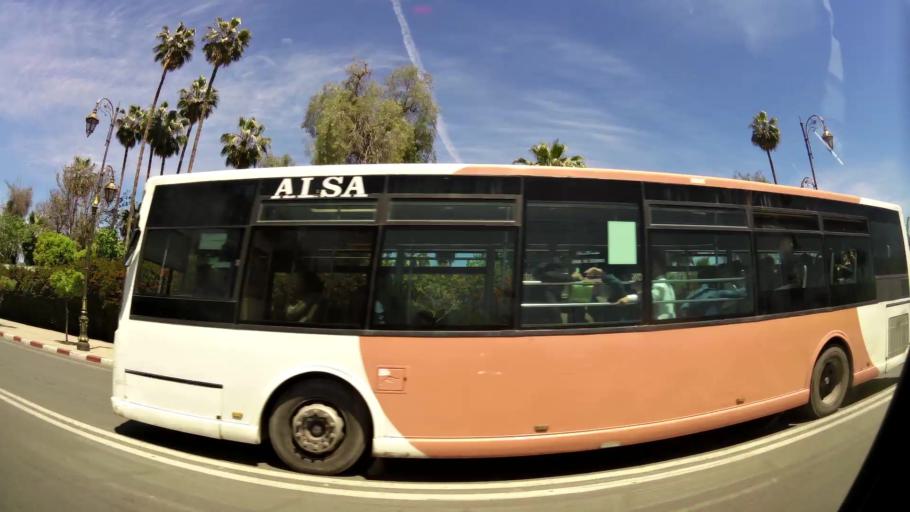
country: MA
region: Marrakech-Tensift-Al Haouz
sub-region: Marrakech
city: Marrakesh
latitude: 31.6260
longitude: -7.9948
